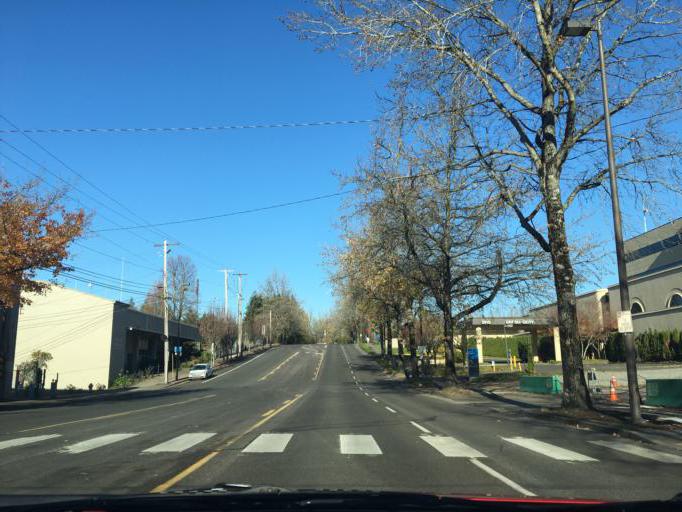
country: US
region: Oregon
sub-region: Multnomah County
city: Portland
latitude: 45.5432
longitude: -122.6719
